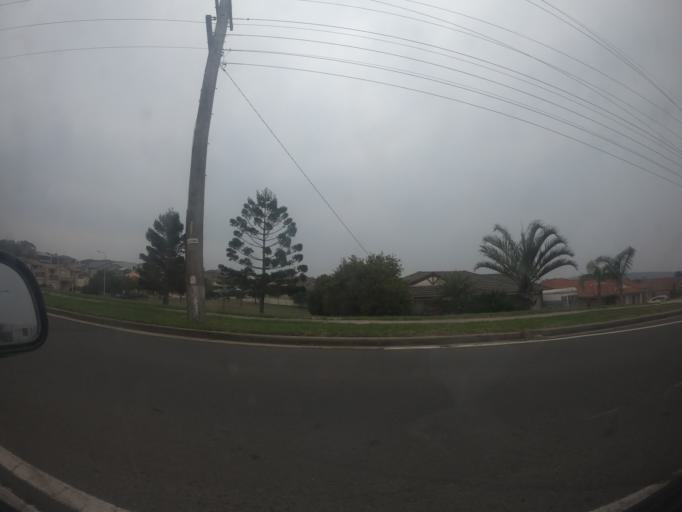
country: AU
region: New South Wales
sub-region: Shellharbour
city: Croom
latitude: -34.5748
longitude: 150.8345
